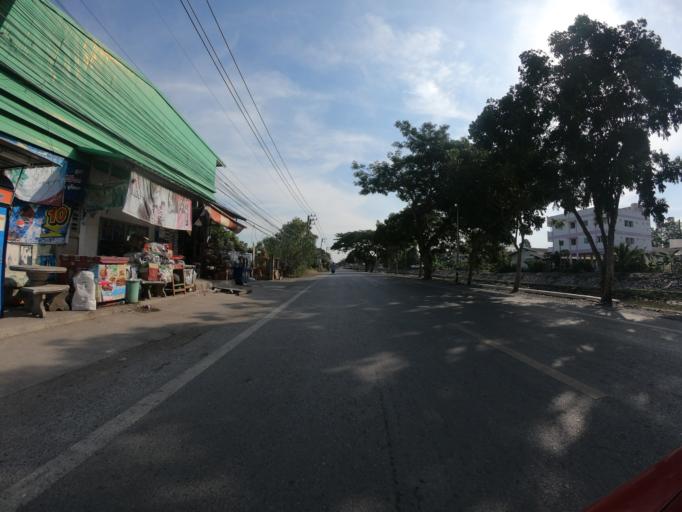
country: TH
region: Pathum Thani
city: Lam Luk Ka
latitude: 13.9676
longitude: 100.7280
